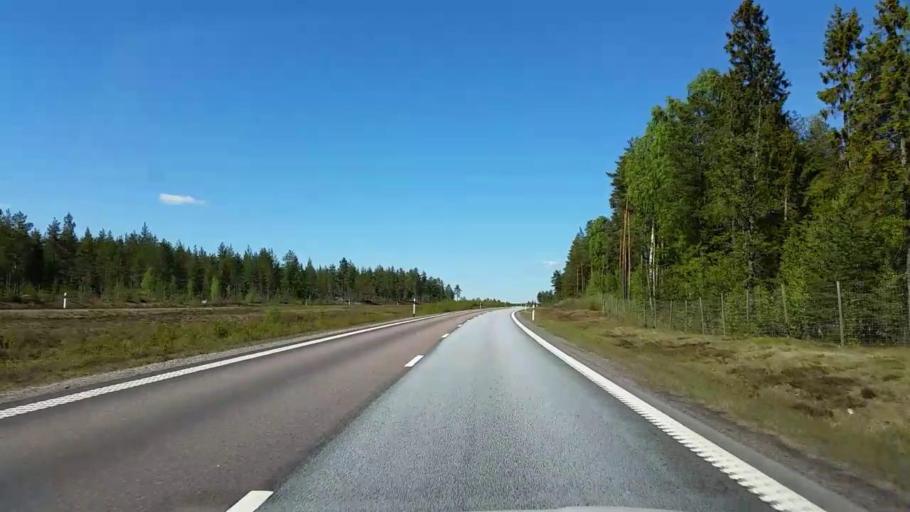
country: SE
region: Gaevleborg
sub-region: Soderhamns Kommun
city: Soderhamn
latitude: 61.3863
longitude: 16.9926
